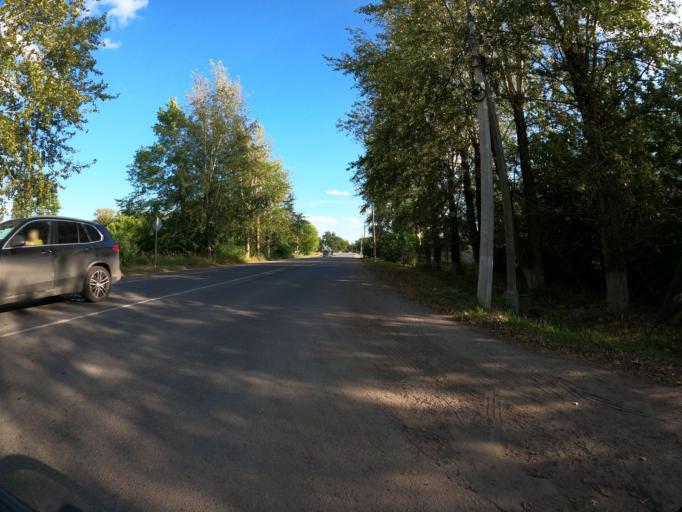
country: RU
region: Moskovskaya
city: Raduzhnyy
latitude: 55.1423
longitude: 38.7315
